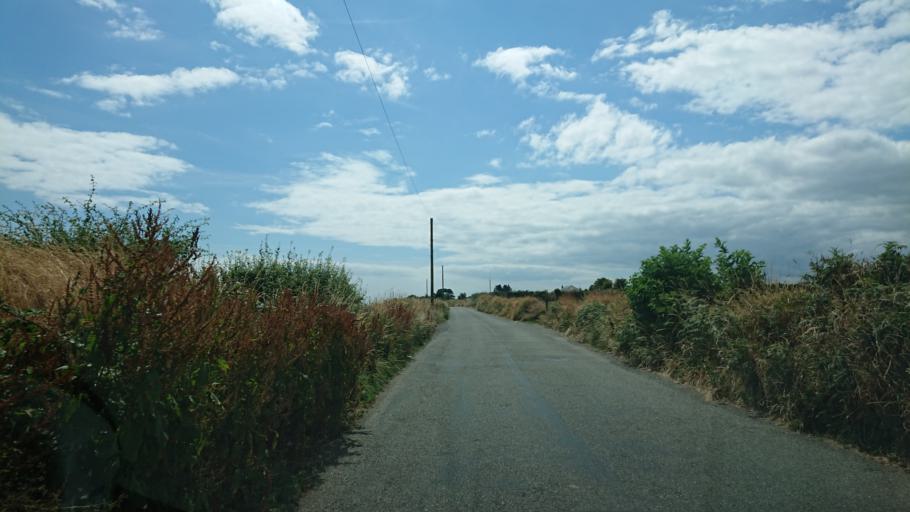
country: IE
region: Munster
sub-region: Waterford
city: Portlaw
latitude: 52.1937
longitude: -7.3288
